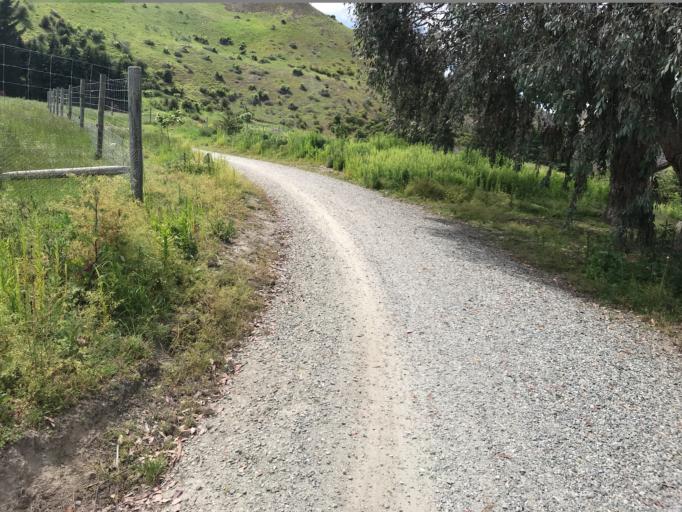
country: NZ
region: Otago
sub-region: Queenstown-Lakes District
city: Arrowtown
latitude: -45.0023
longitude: 168.8756
